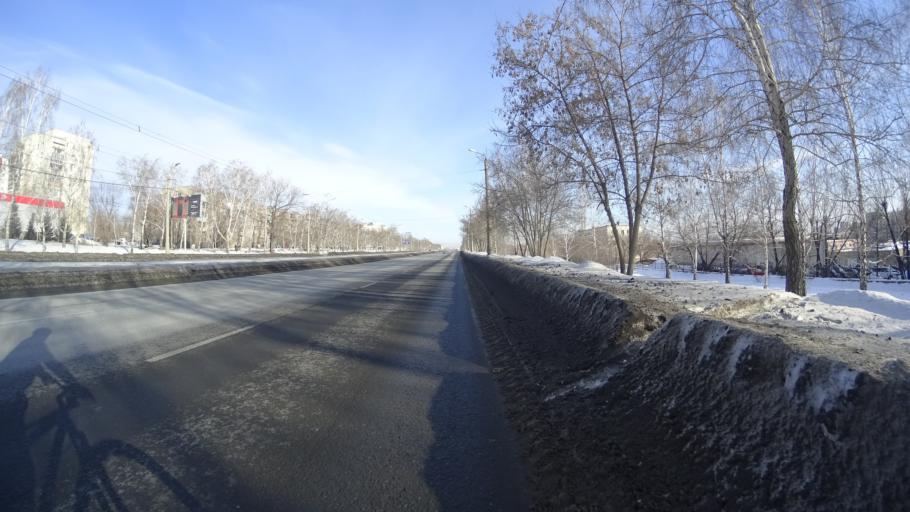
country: RU
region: Chelyabinsk
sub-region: Gorod Chelyabinsk
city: Chelyabinsk
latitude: 55.1889
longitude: 61.3407
